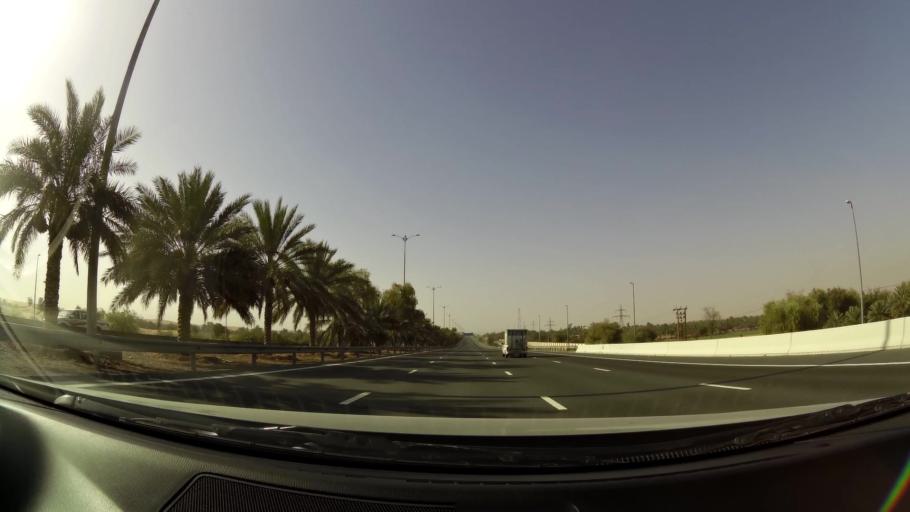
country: OM
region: Al Buraimi
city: Al Buraymi
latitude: 24.4271
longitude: 55.7890
